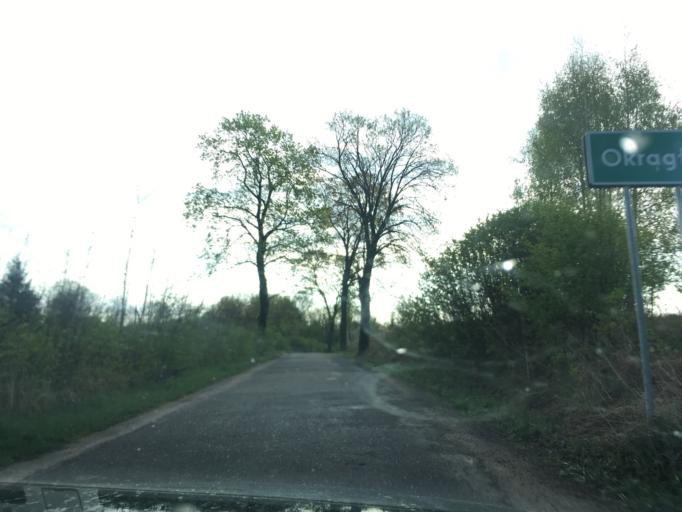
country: PL
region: Warmian-Masurian Voivodeship
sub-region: Powiat ostrodzki
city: Dabrowno
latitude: 53.4279
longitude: 20.0131
